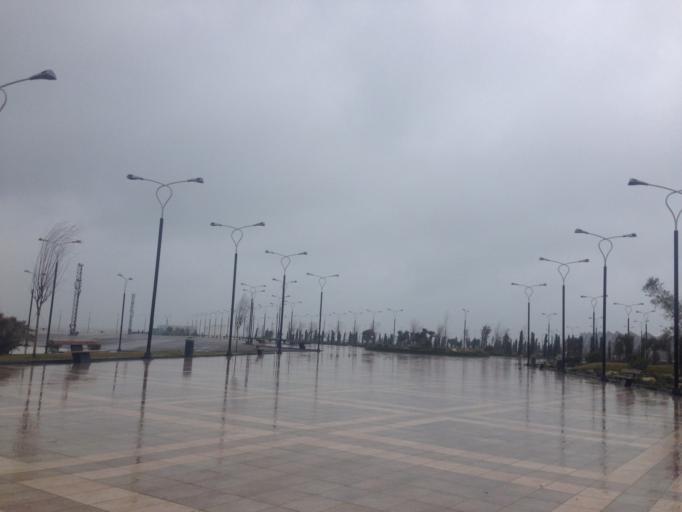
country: AZ
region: Baki
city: Badamdar
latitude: 40.3467
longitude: 49.8423
